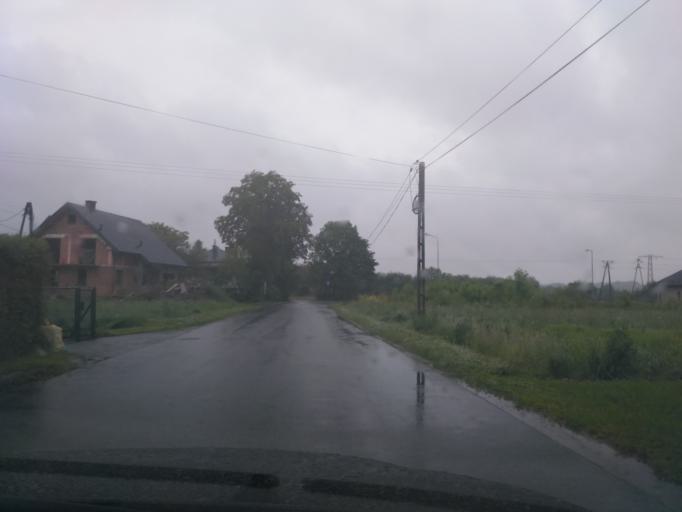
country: PL
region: Subcarpathian Voivodeship
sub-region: Powiat jasielski
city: Jaslo
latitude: 49.7420
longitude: 21.4987
